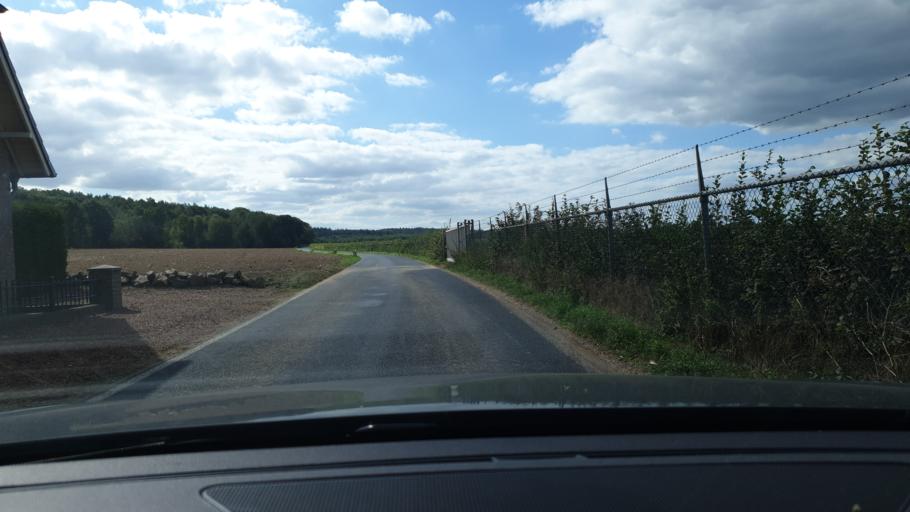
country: DE
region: North Rhine-Westphalia
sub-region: Regierungsbezirk Dusseldorf
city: Kranenburg
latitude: 51.7751
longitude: 5.9939
